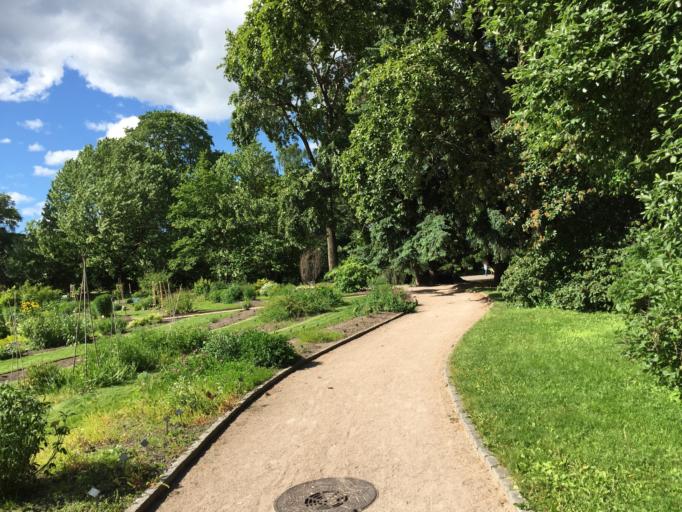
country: NO
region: Oslo
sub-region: Oslo
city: Oslo
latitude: 59.9185
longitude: 10.7729
